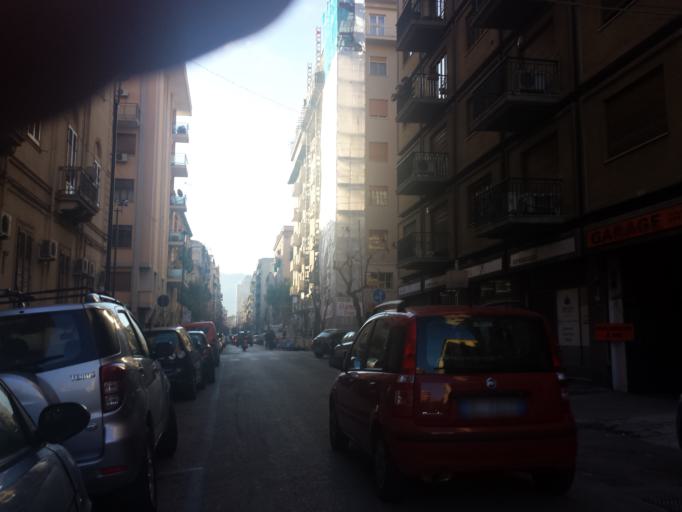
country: IT
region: Sicily
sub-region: Palermo
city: Palermo
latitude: 38.1283
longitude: 13.3510
